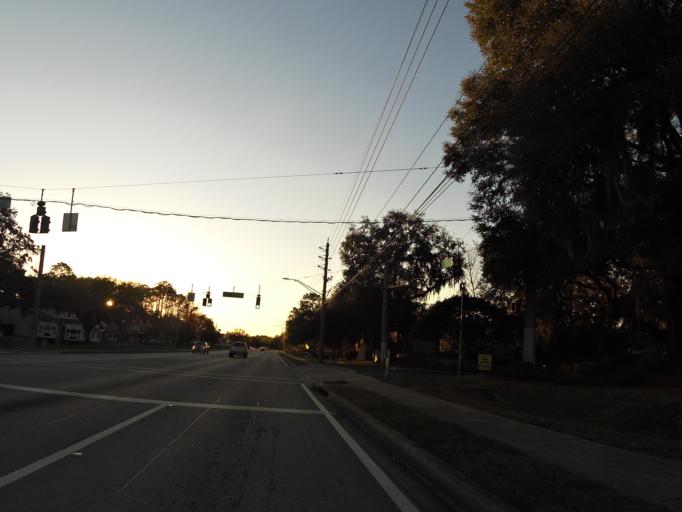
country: US
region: Florida
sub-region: Saint Johns County
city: Fruit Cove
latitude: 30.2058
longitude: -81.6124
